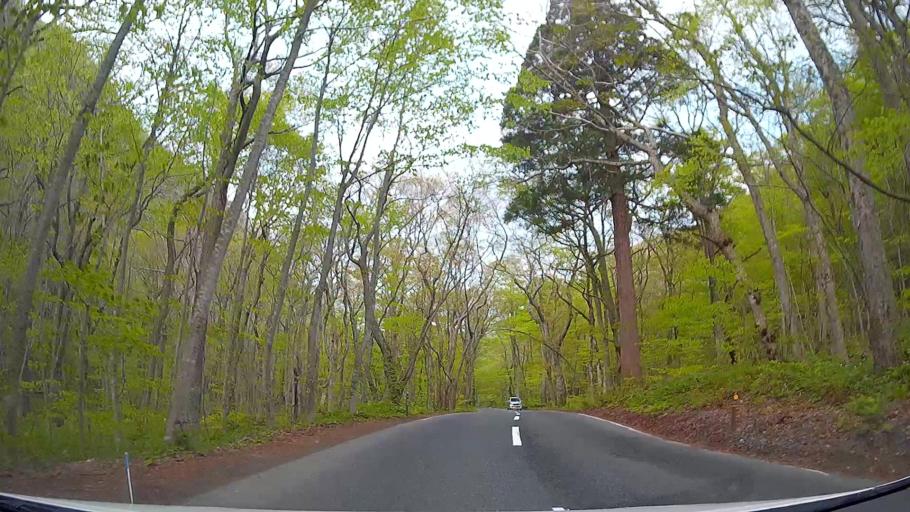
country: JP
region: Akita
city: Hanawa
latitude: 40.4832
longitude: 140.9458
